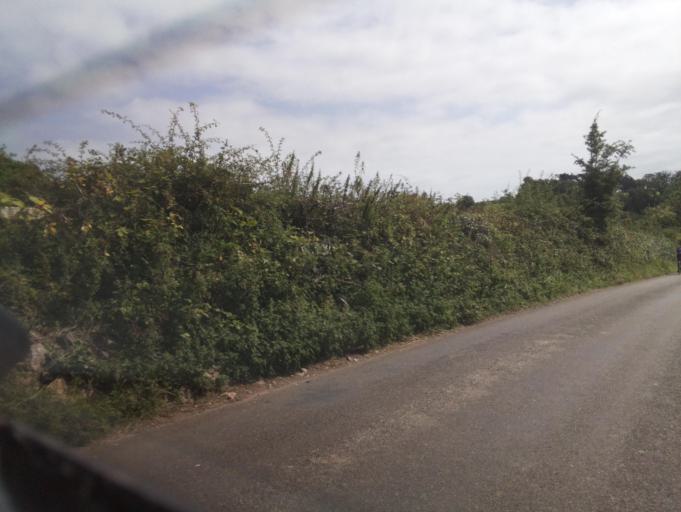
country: GB
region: England
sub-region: Borough of Torbay
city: Paignton
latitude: 50.4009
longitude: -3.5851
